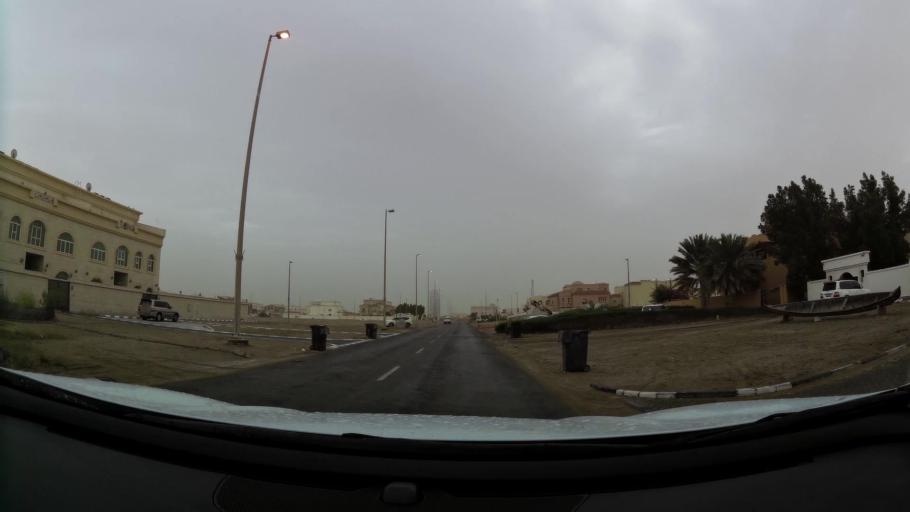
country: AE
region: Abu Dhabi
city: Abu Dhabi
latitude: 24.4268
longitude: 54.5814
